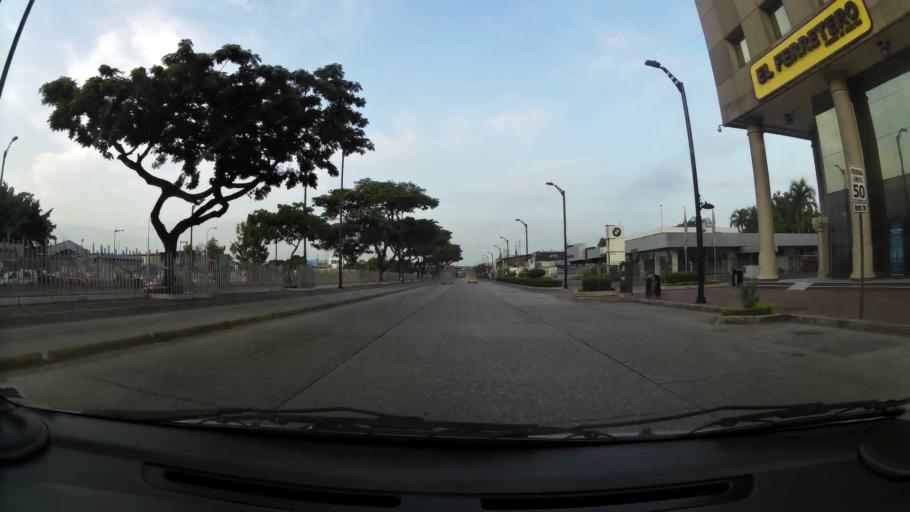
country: EC
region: Guayas
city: Eloy Alfaro
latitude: -2.1600
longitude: -79.8894
